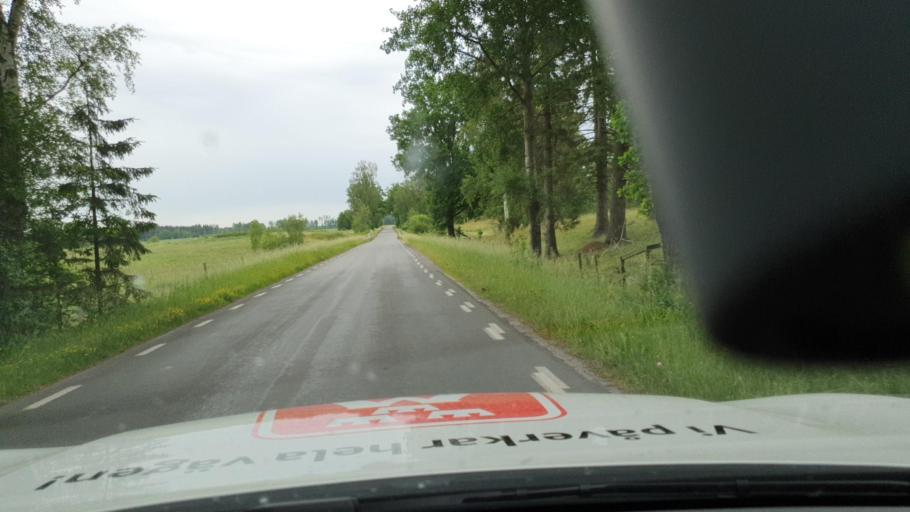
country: SE
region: Vaestra Goetaland
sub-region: Tibro Kommun
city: Tibro
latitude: 58.3261
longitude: 14.0992
